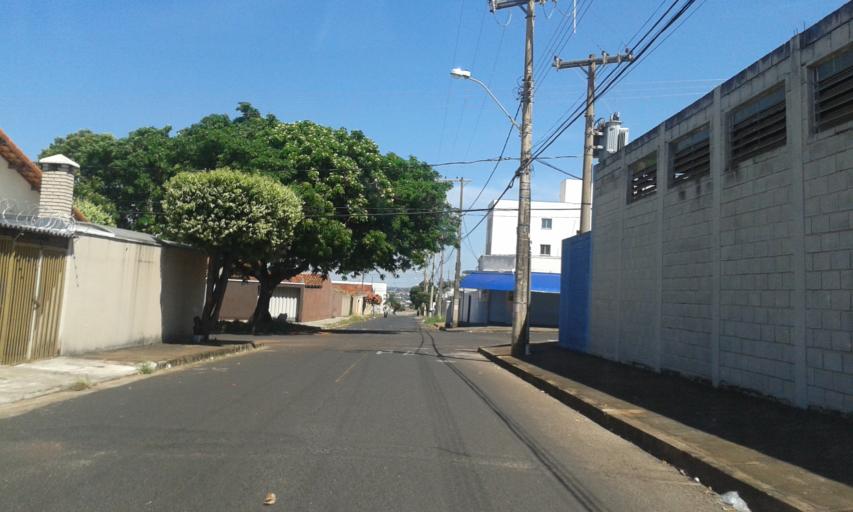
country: BR
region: Minas Gerais
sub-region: Uberlandia
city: Uberlandia
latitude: -18.9298
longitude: -48.2497
